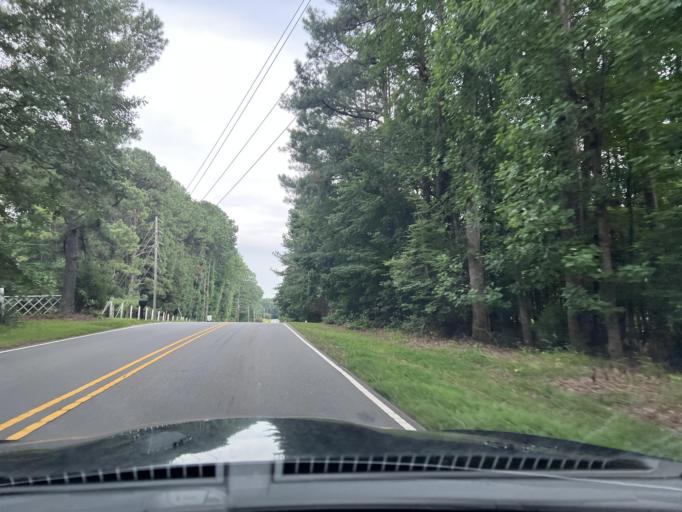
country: US
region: North Carolina
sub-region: Wake County
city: Wake Forest
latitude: 36.0113
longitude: -78.5416
